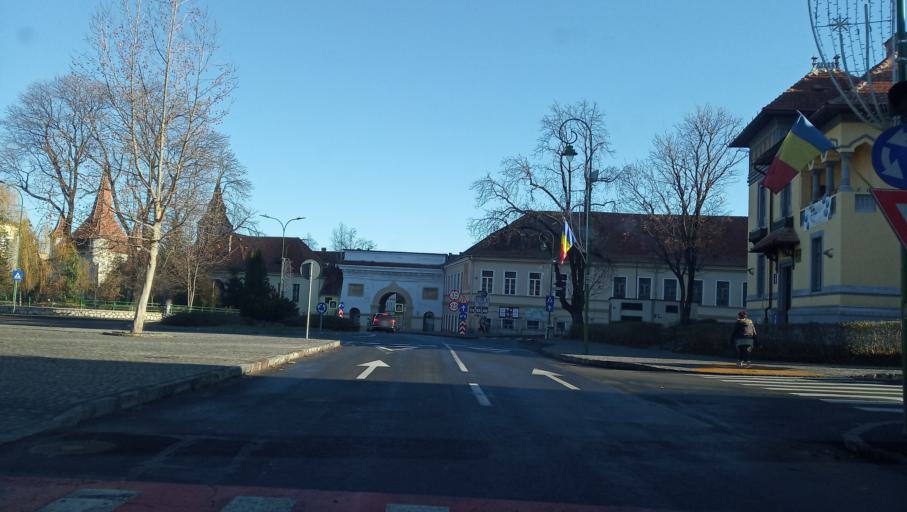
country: RO
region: Brasov
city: Brasov
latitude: 45.6386
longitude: 25.5855
